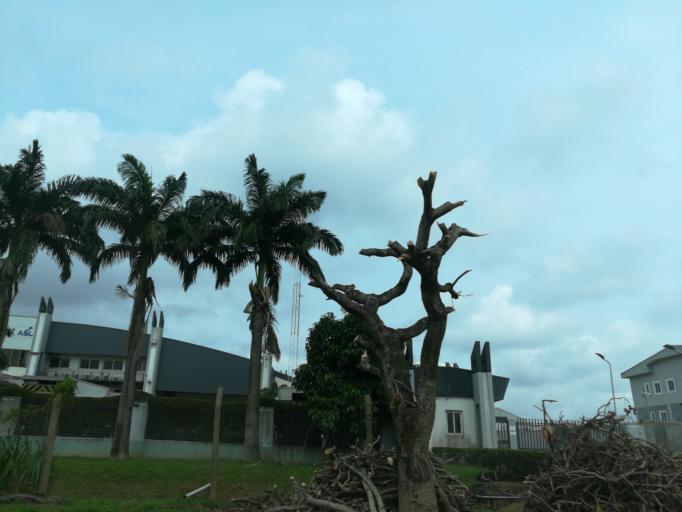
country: NG
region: Lagos
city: Oshodi
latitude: 6.5690
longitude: 3.3237
